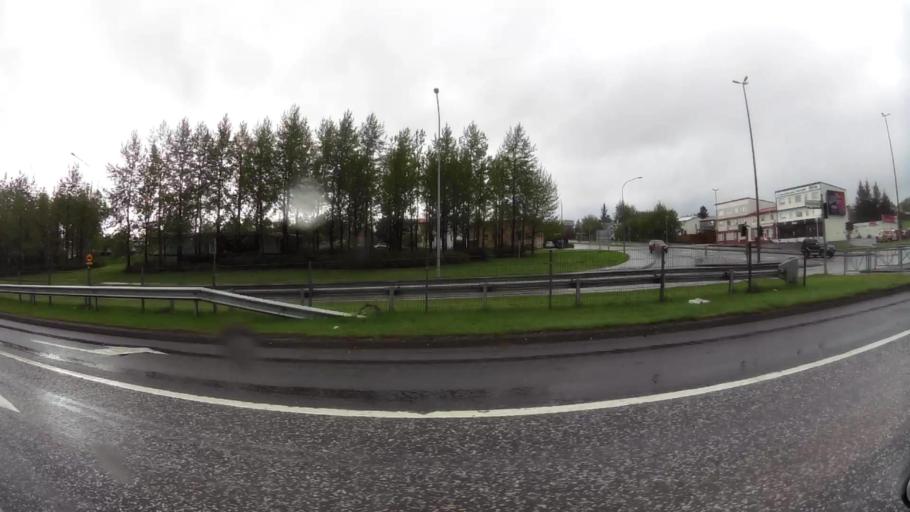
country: IS
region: Capital Region
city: Reykjavik
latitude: 64.1295
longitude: -21.8750
